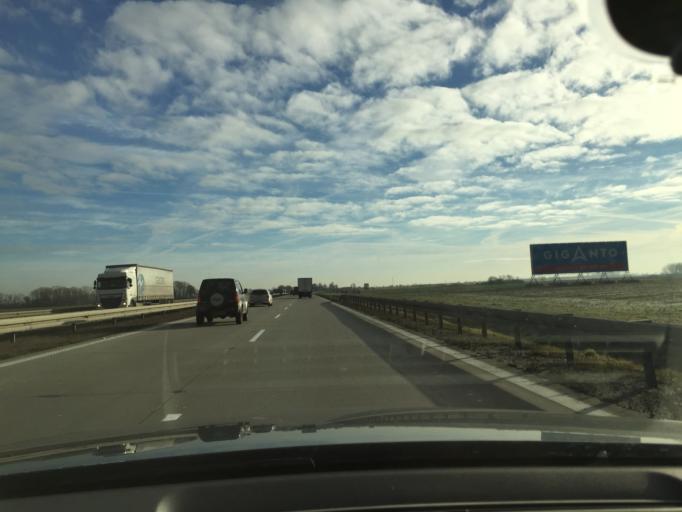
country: PL
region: Lower Silesian Voivodeship
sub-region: Powiat sredzki
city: Ciechow
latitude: 51.0559
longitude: 16.5378
